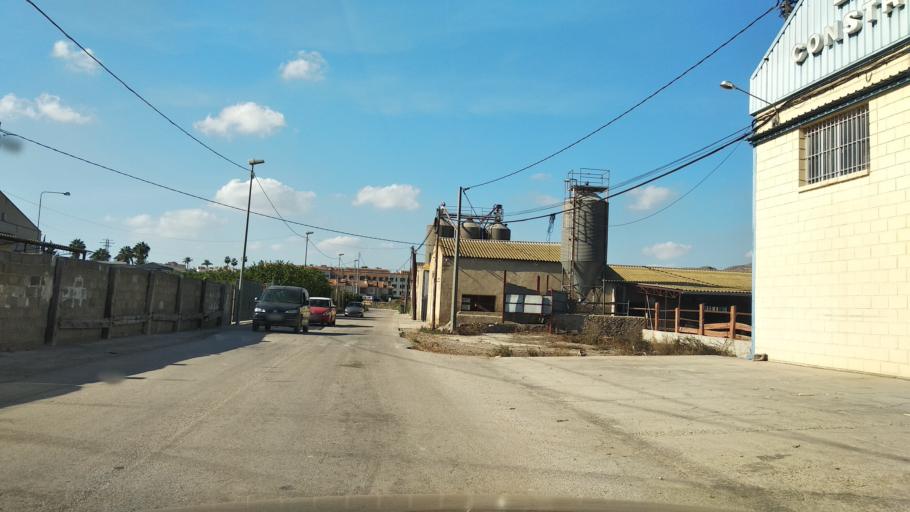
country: ES
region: Murcia
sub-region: Murcia
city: Santomera
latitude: 38.0566
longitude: -1.0436
